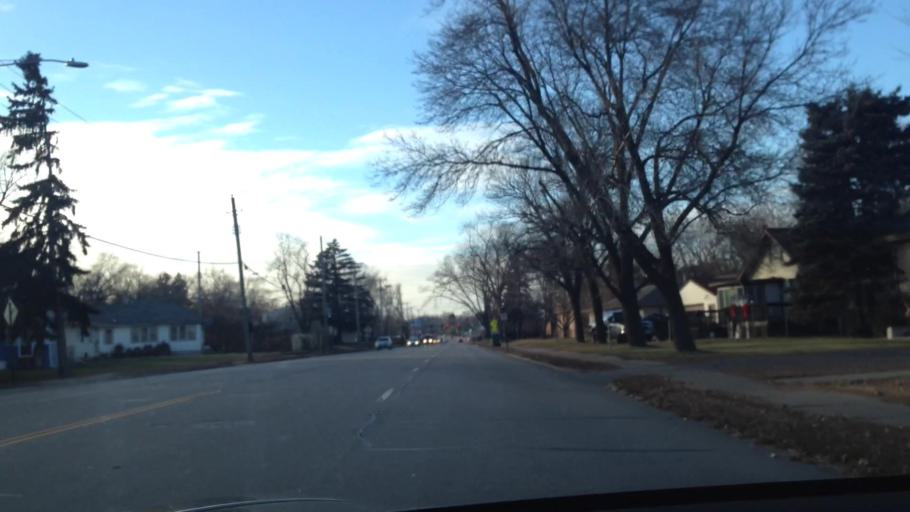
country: US
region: Minnesota
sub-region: Hennepin County
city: Crystal
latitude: 45.0316
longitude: -93.3518
